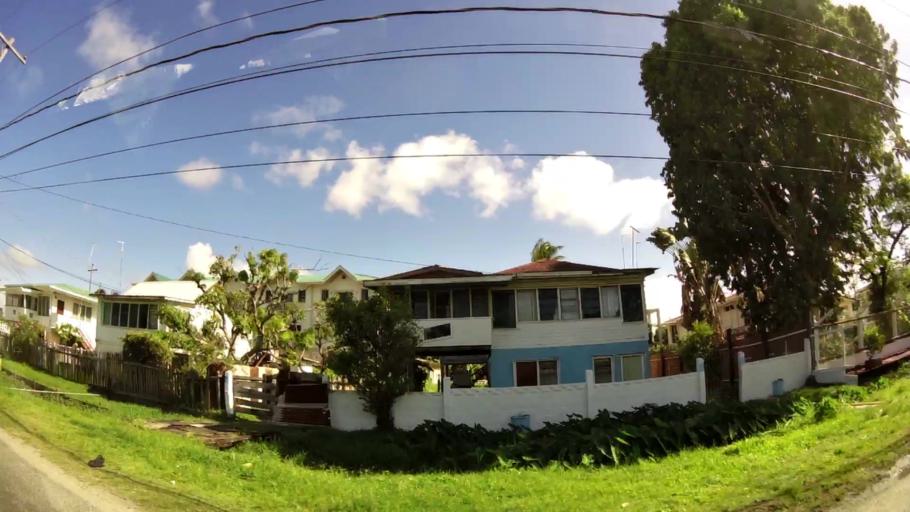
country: GY
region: Demerara-Mahaica
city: Georgetown
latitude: 6.8220
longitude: -58.1274
